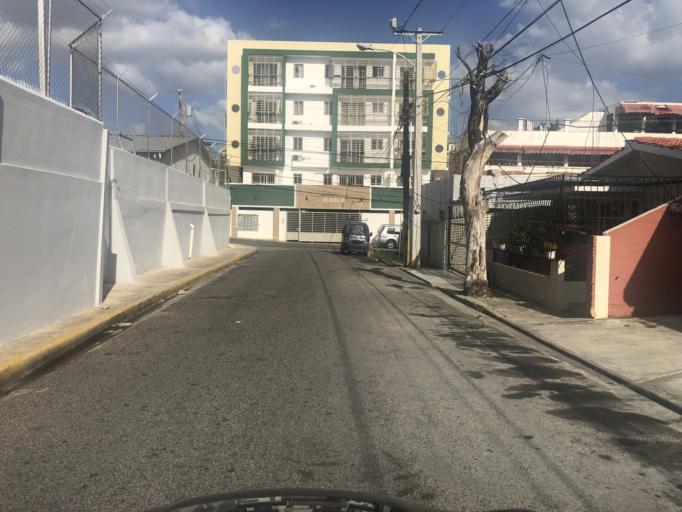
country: DO
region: Nacional
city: La Julia
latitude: 18.4554
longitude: -69.9277
